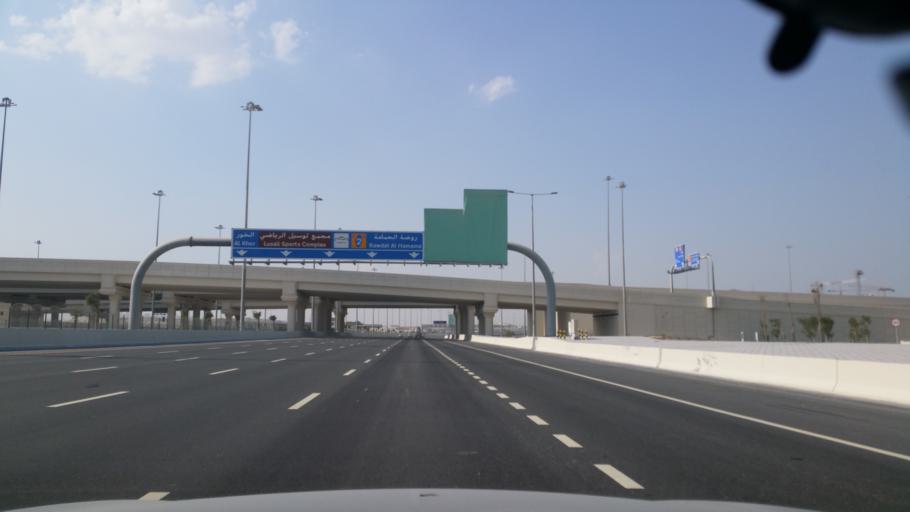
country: QA
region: Baladiyat Umm Salal
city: Umm Salal Muhammad
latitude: 25.4028
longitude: 51.4925
